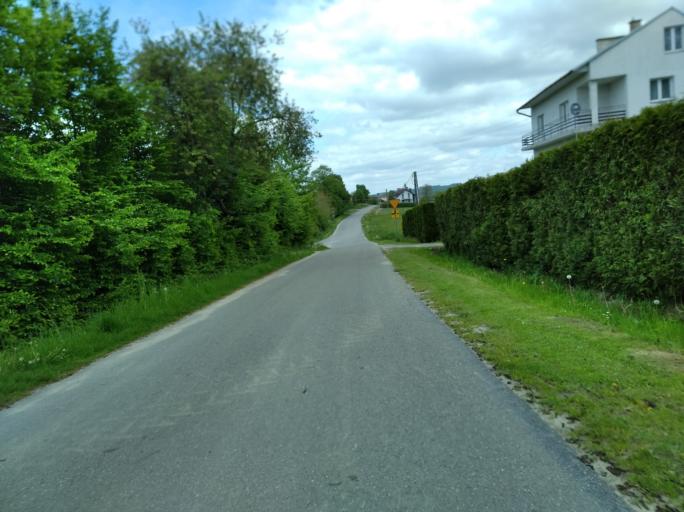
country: PL
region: Subcarpathian Voivodeship
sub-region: Powiat ropczycko-sedziszowski
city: Wielopole Skrzynskie
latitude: 49.9332
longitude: 21.6009
